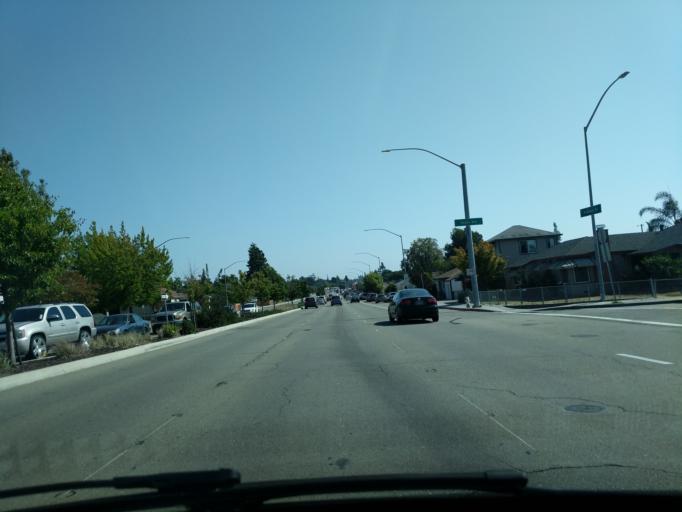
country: US
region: California
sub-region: Alameda County
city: Castro Valley
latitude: 37.6896
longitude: -122.0737
